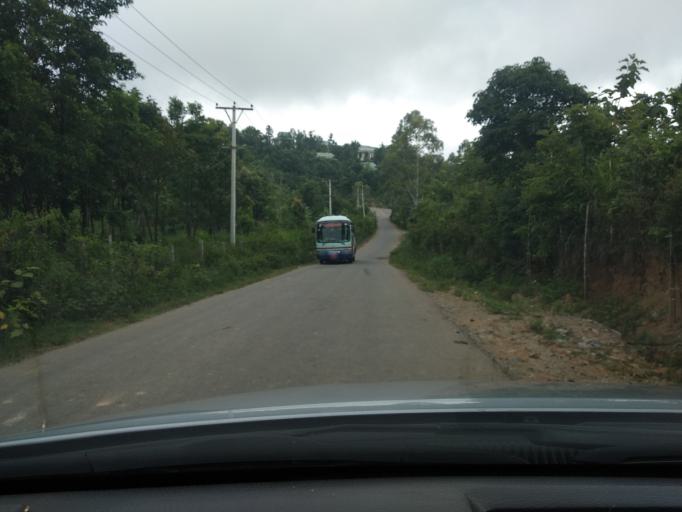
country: MM
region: Mandalay
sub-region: Pyin Oo Lwin District
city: Pyin Oo Lwin
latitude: 21.9155
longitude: 96.3834
